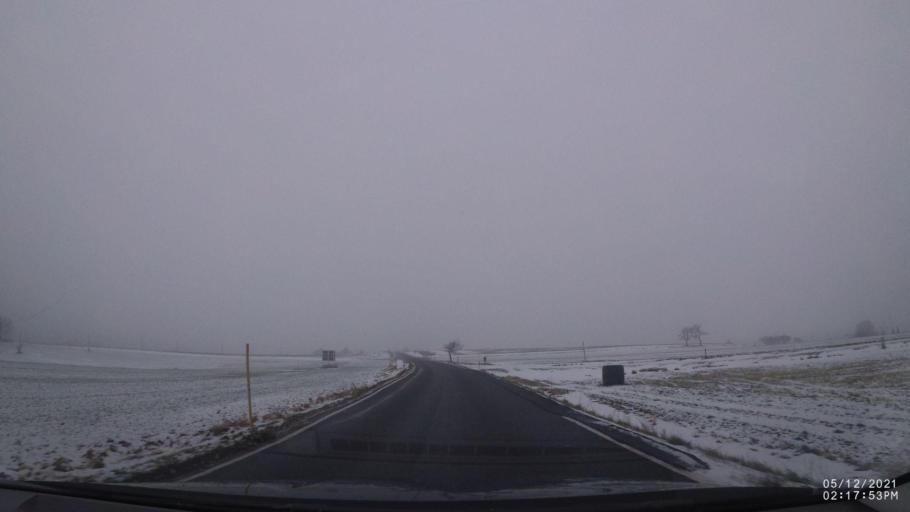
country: CZ
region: Kralovehradecky
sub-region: Okres Nachod
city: Cerveny Kostelec
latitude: 50.4606
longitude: 16.1297
